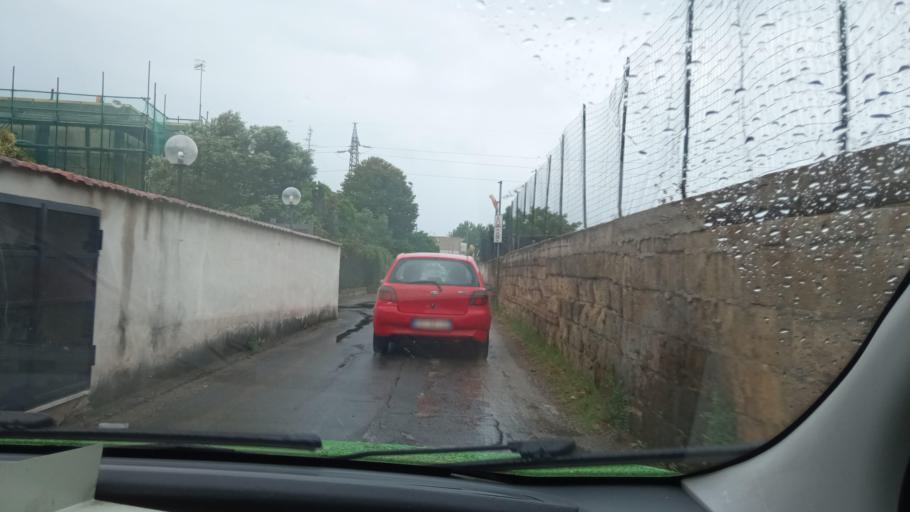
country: IT
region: Campania
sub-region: Provincia di Napoli
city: Pozzuoli
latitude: 40.8425
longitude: 14.1178
